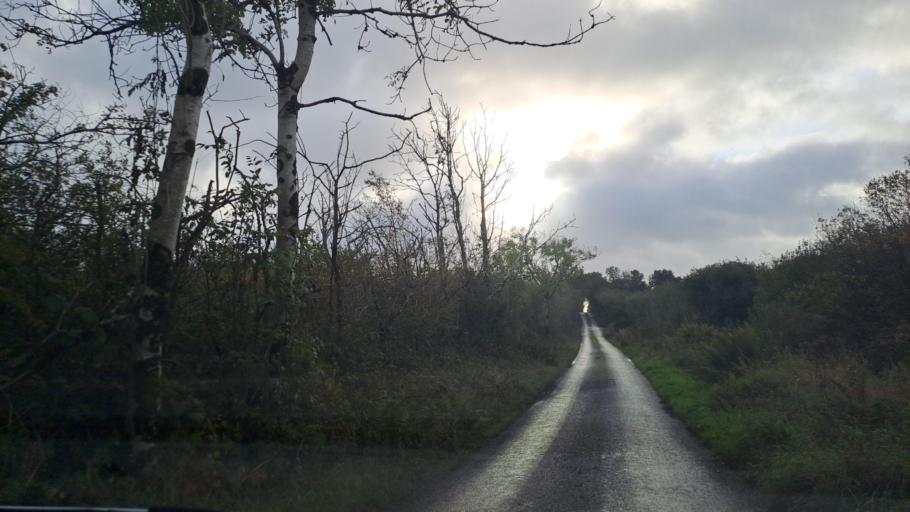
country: IE
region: Ulster
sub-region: An Cabhan
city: Kingscourt
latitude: 53.9634
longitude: -6.8256
